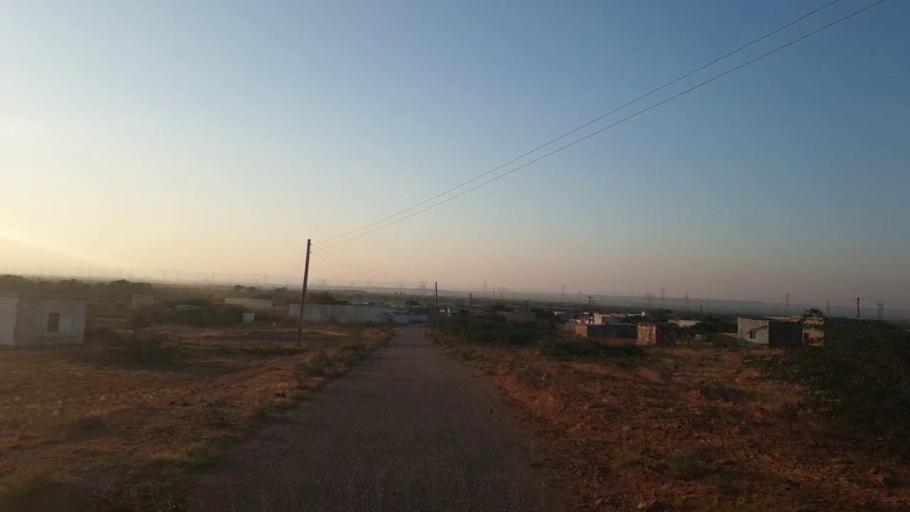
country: PK
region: Sindh
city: Gharo
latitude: 25.1664
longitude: 67.6688
